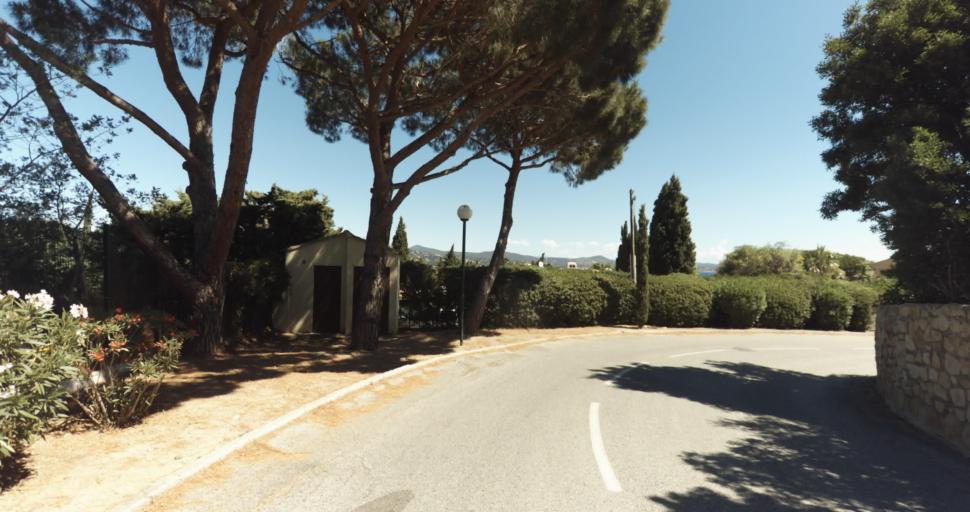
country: FR
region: Provence-Alpes-Cote d'Azur
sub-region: Departement du Var
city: Saint-Tropez
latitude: 43.2628
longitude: 6.6114
